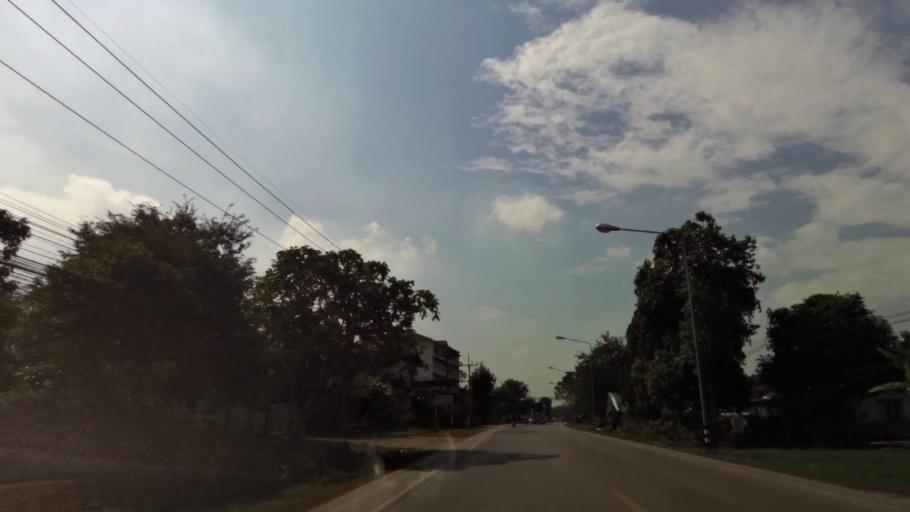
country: TH
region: Chiang Rai
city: Chiang Rai
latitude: 19.8590
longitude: 99.7631
